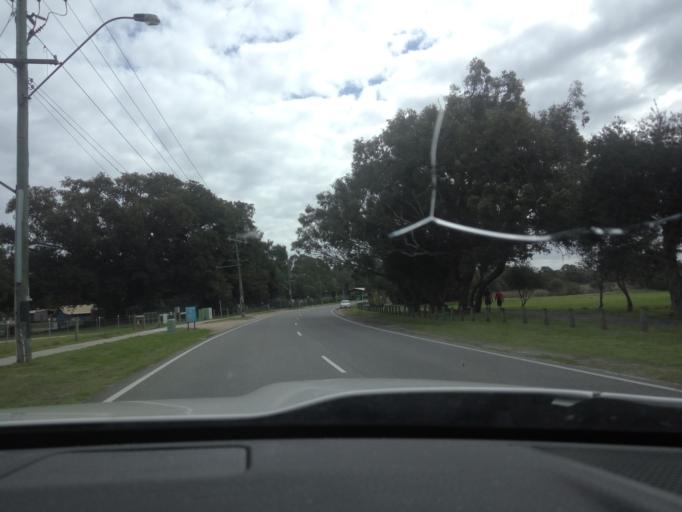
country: AU
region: Western Australia
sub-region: City of Cockburn
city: Bibra Lake
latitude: -32.0986
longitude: 115.8207
